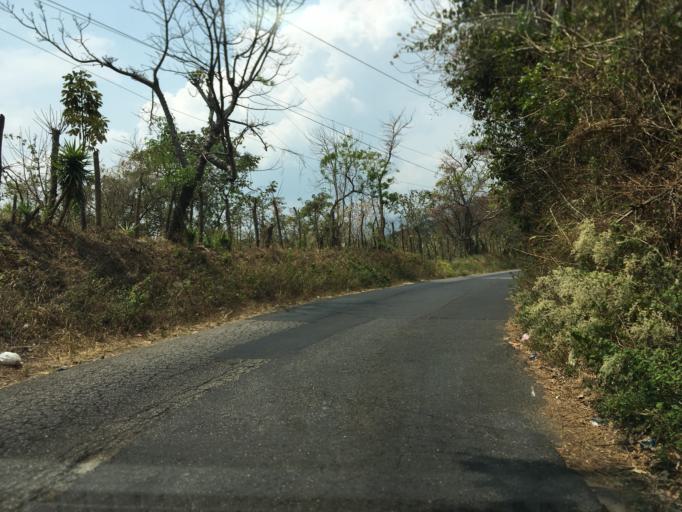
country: GT
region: Escuintla
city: San Vicente Pacaya
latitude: 14.3869
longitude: -90.5514
